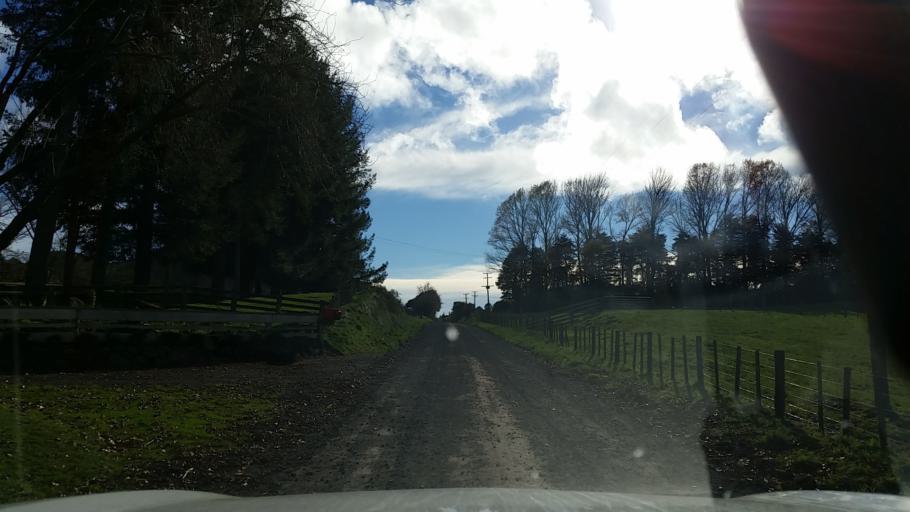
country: NZ
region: Bay of Plenty
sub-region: Rotorua District
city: Rotorua
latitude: -38.3715
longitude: 176.2067
